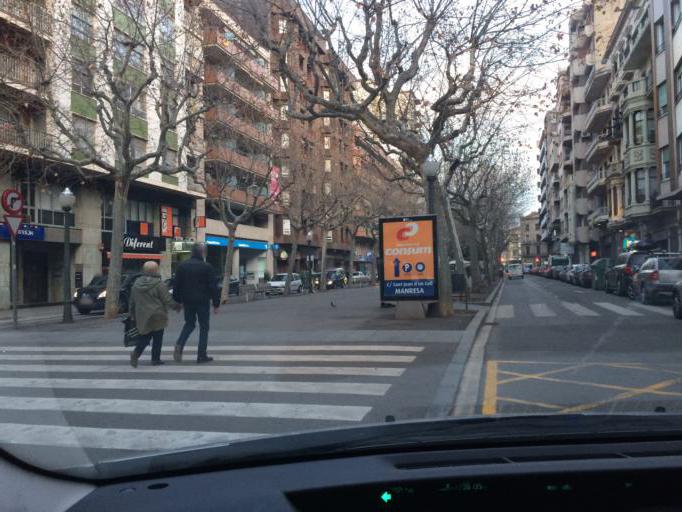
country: ES
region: Catalonia
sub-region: Provincia de Barcelona
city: Manresa
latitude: 41.7302
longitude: 1.8292
